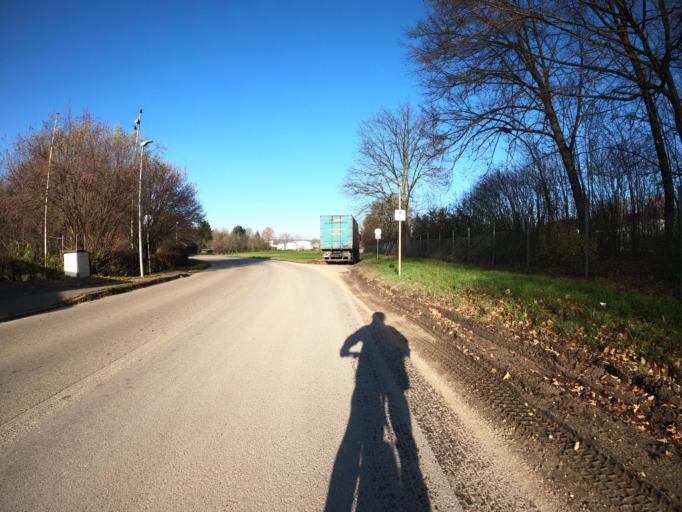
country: DE
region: Baden-Wuerttemberg
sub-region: Regierungsbezirk Stuttgart
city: Goeppingen
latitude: 48.6853
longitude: 9.6710
